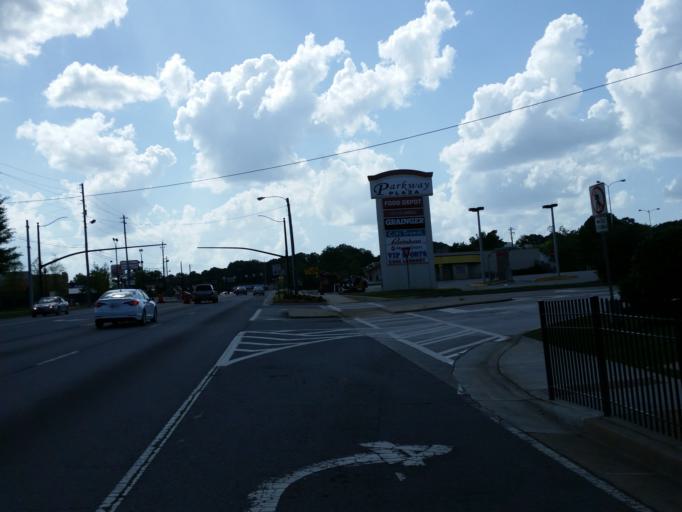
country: US
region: Georgia
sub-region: Cobb County
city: Marietta
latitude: 33.9427
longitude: -84.5319
